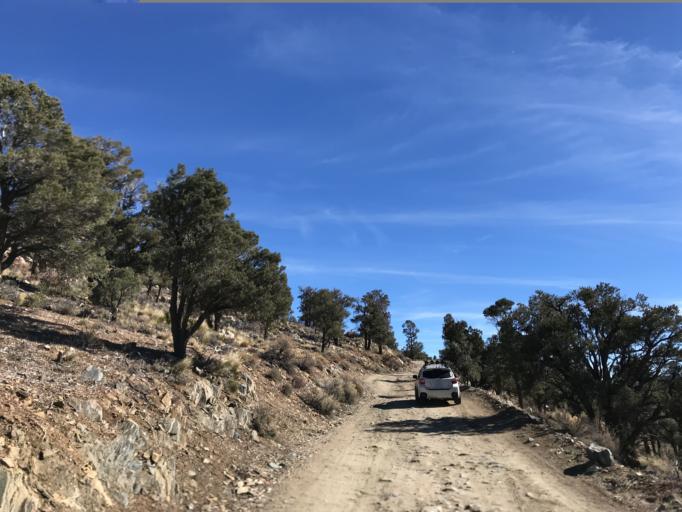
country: US
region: California
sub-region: San Bernardino County
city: Big Bear City
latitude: 34.2728
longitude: -116.7842
